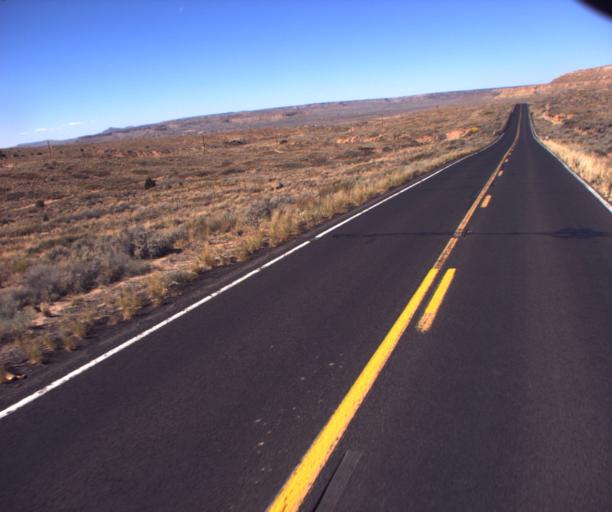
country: US
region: Arizona
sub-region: Navajo County
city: First Mesa
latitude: 35.8681
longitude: -110.5465
